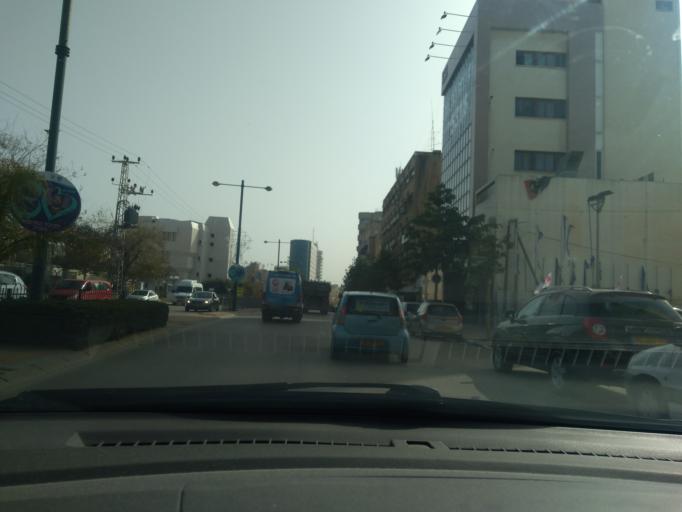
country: IL
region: Central District
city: Netanya
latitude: 32.3287
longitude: 34.8619
